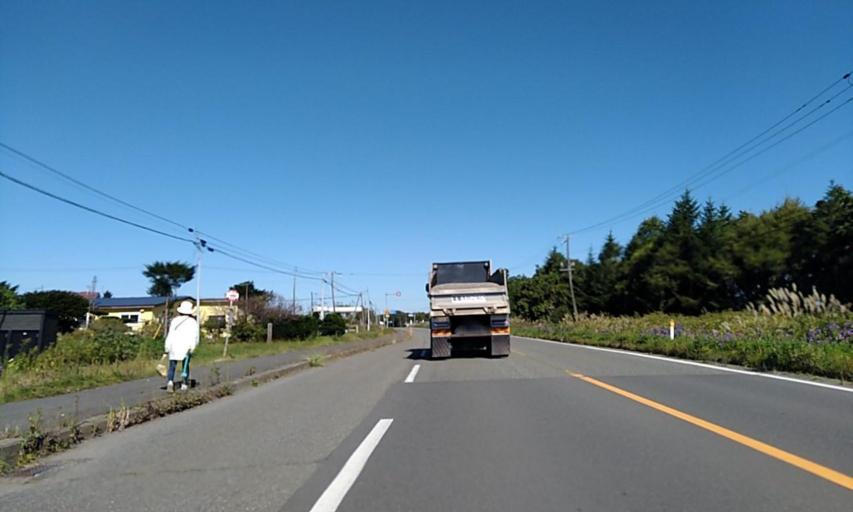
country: JP
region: Hokkaido
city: Shizunai-furukawacho
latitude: 42.4953
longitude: 142.0554
